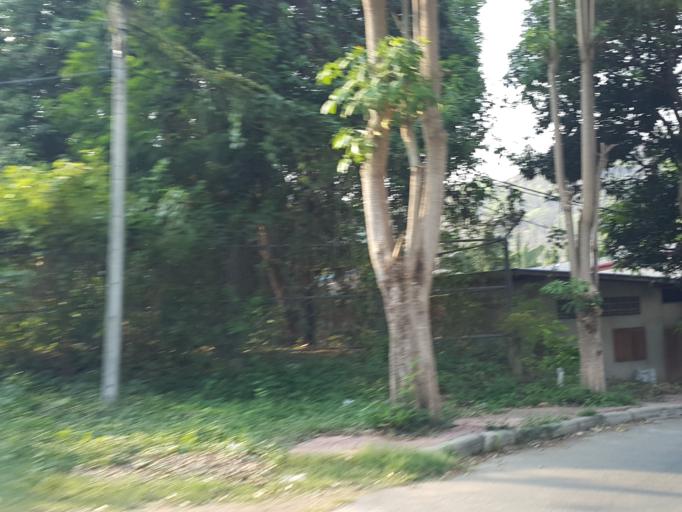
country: TH
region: Kanchanaburi
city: Si Sawat
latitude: 14.3827
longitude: 99.1362
